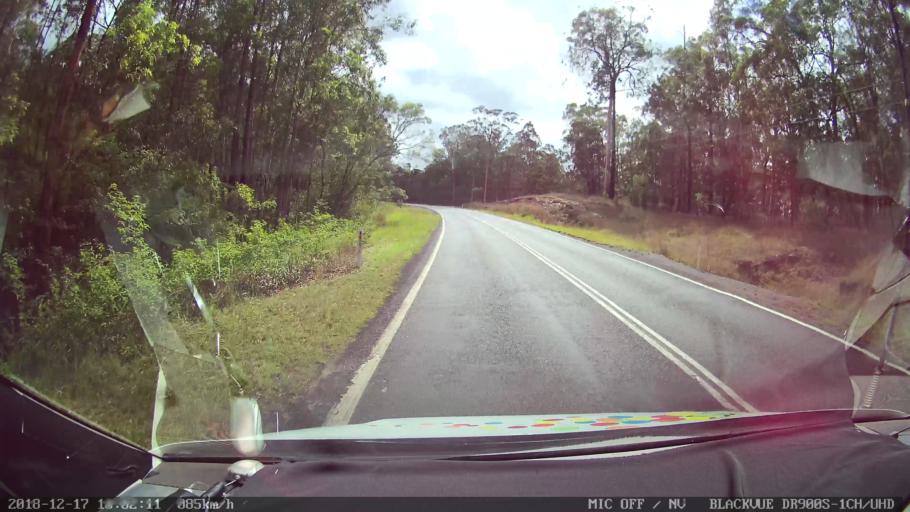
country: AU
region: New South Wales
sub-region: Tenterfield Municipality
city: Carrolls Creek
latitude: -28.9037
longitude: 152.4486
